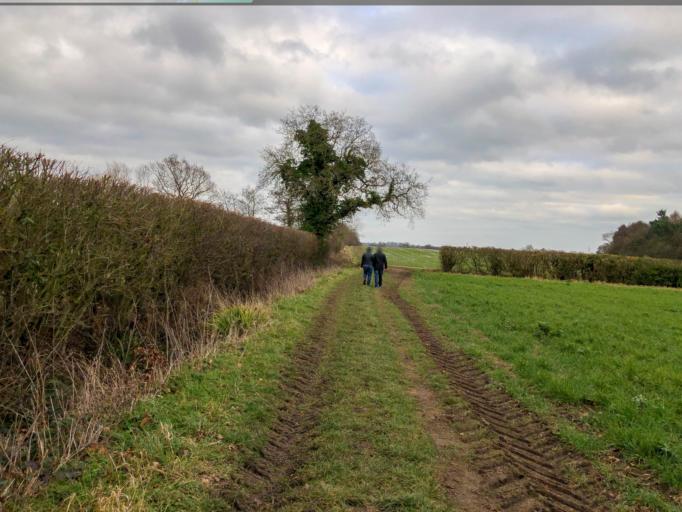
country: GB
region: England
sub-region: Warwickshire
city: Wroxall
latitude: 52.3501
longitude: -1.6324
